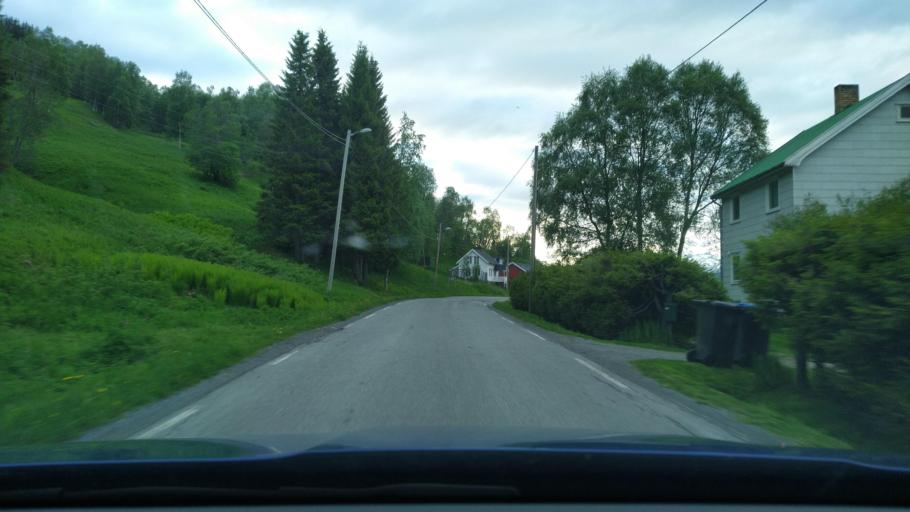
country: NO
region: Troms
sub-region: Sorreisa
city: Sorreisa
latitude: 69.1378
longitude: 18.0580
